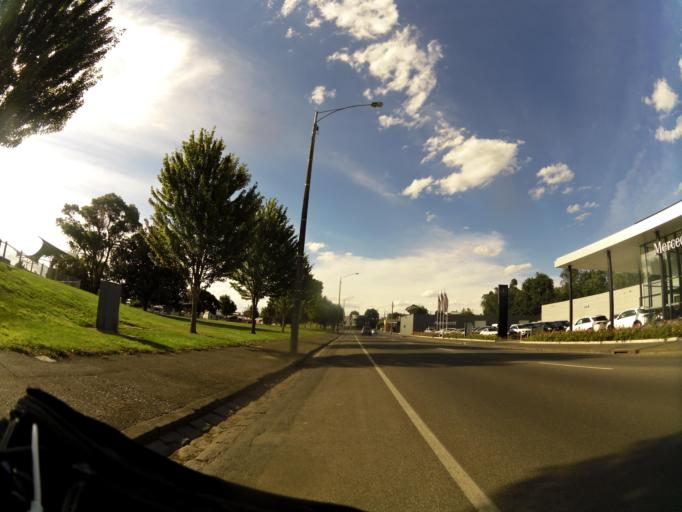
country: AU
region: Victoria
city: Ballarat East
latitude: -37.5666
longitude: 143.8682
